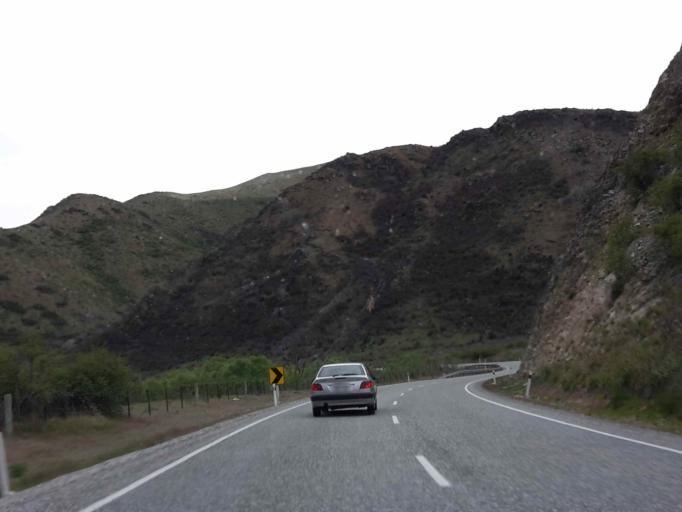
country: NZ
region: Otago
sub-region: Queenstown-Lakes District
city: Wanaka
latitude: -44.7347
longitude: 169.5072
